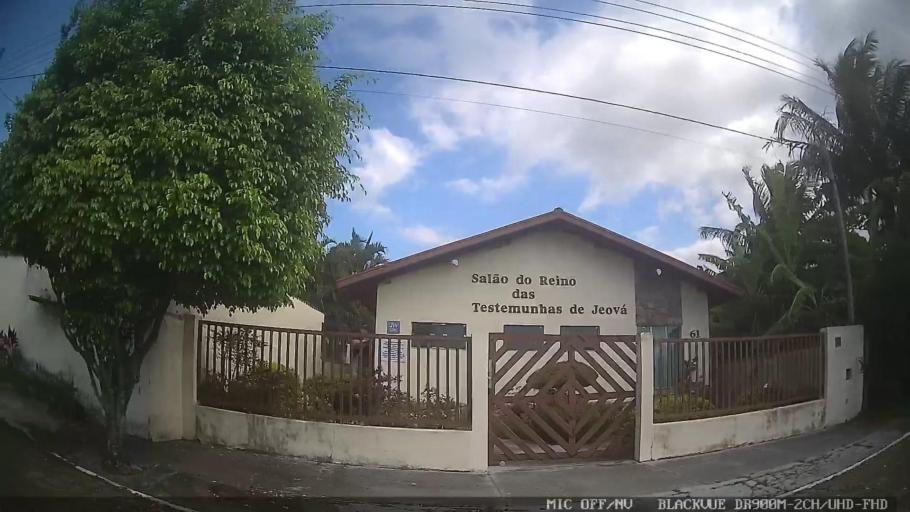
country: BR
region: Sao Paulo
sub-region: Sao Sebastiao
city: Sao Sebastiao
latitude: -23.7144
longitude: -45.4268
